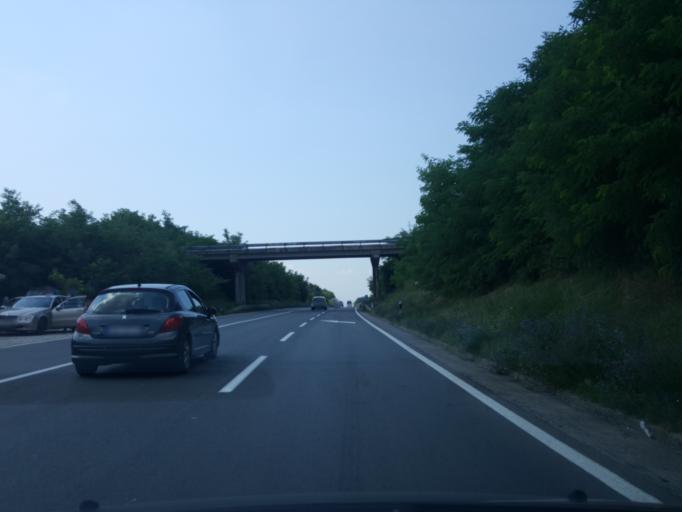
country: RS
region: Central Serbia
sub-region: Belgrade
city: Sopot
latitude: 44.5391
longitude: 20.6585
